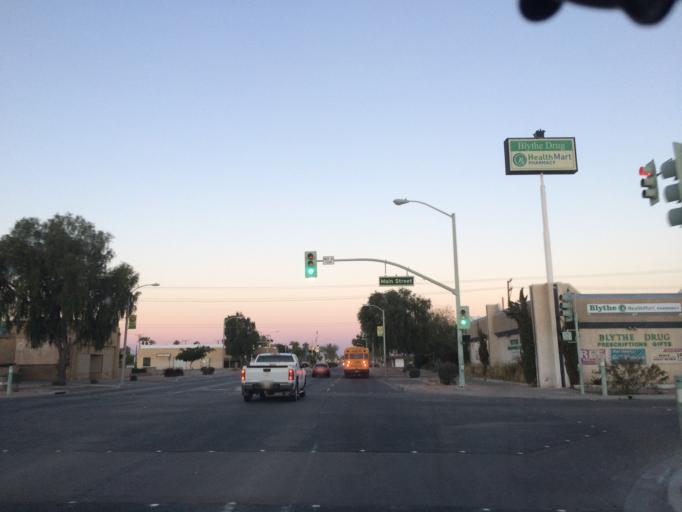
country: US
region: California
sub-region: Riverside County
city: Blythe
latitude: 33.6104
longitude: -114.5993
